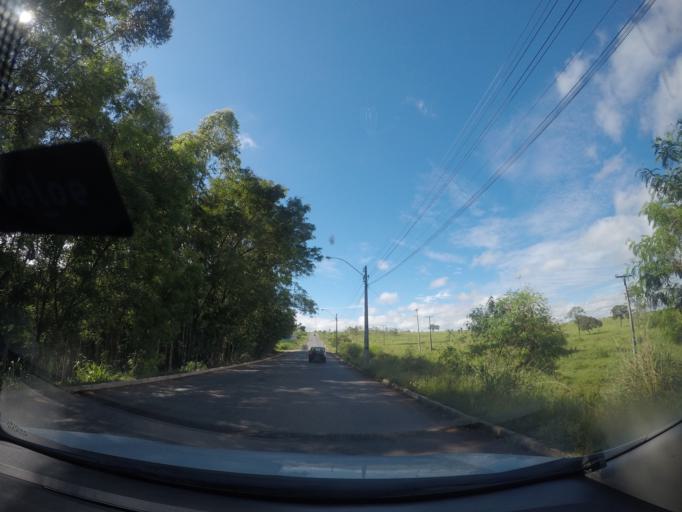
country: BR
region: Goias
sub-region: Senador Canedo
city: Senador Canedo
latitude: -16.6606
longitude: -49.1522
